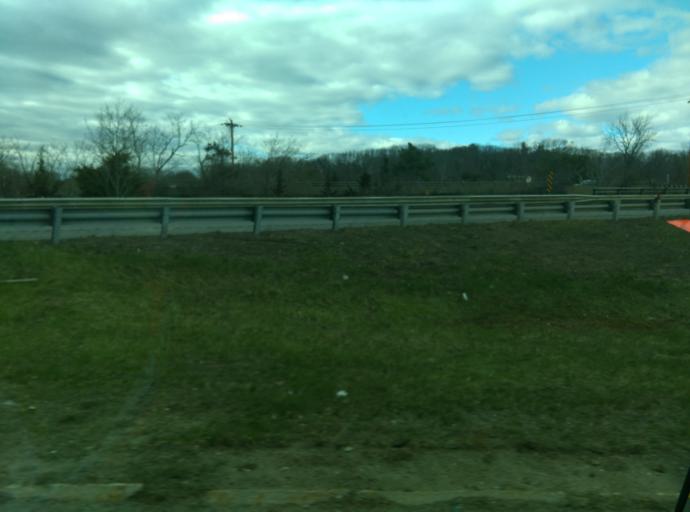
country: US
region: Massachusetts
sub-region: Essex County
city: Amesbury
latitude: 42.8462
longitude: -70.9195
